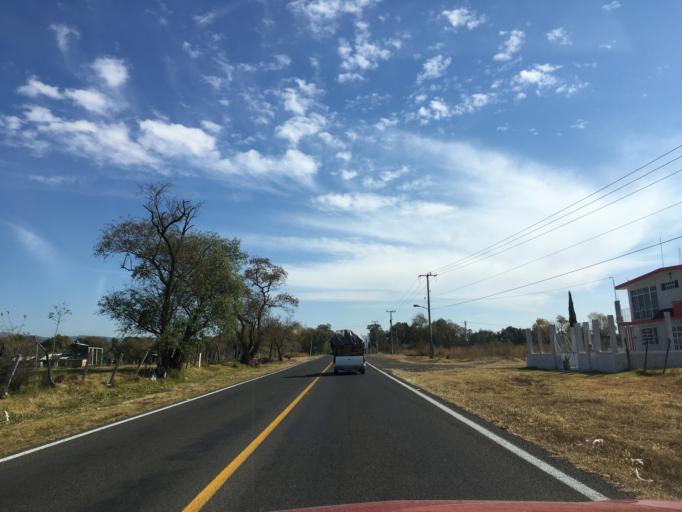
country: MX
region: Michoacan
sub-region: Hidalgo
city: San Lucas Huarirapeo (La Mesa de San Lucas)
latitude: 19.6874
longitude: -100.6288
